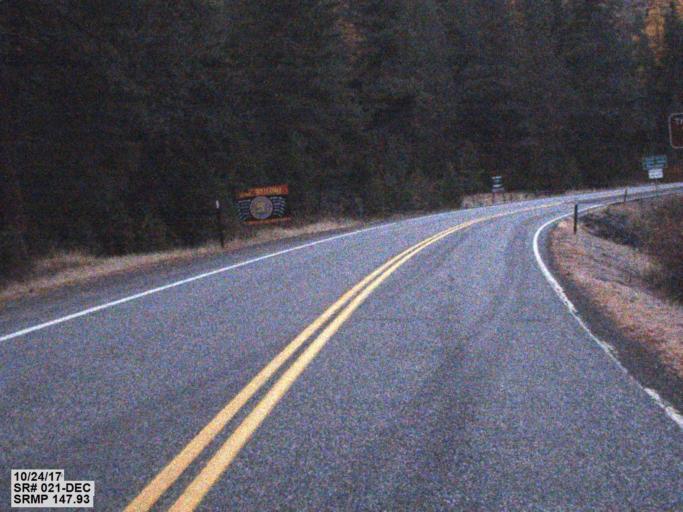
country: US
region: Washington
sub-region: Ferry County
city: Republic
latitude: 48.4813
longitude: -118.7289
